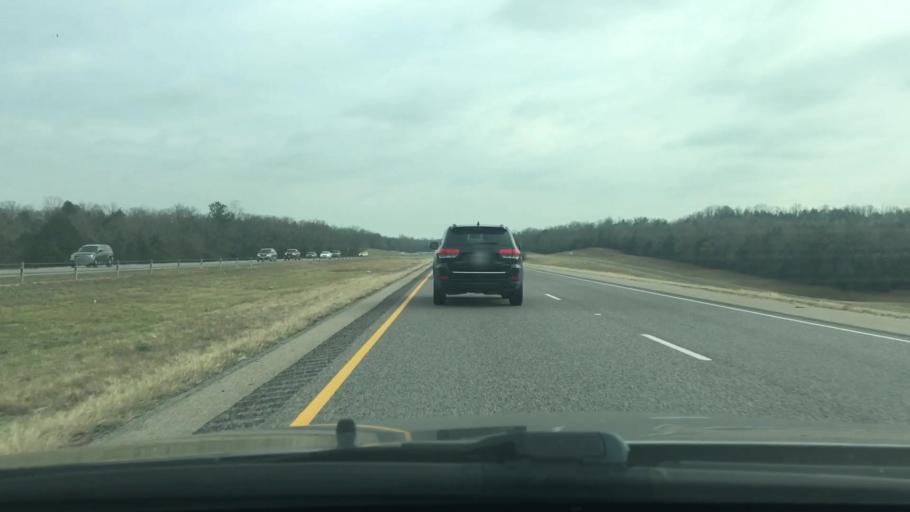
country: US
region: Texas
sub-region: Leon County
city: Buffalo
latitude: 31.5118
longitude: -96.1041
